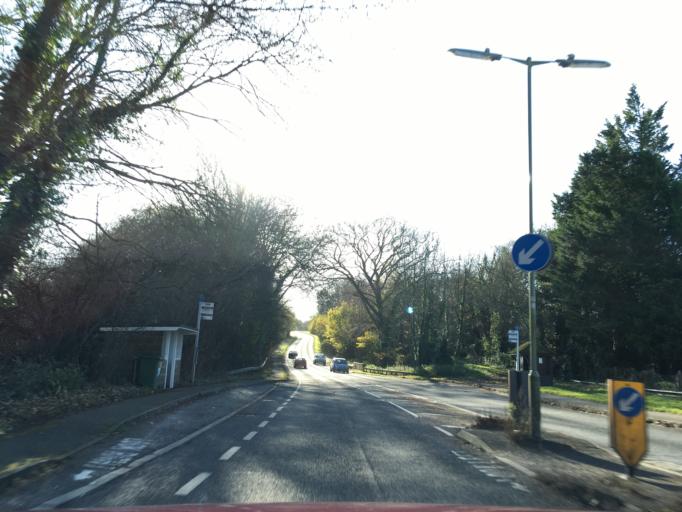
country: GB
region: England
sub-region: Hampshire
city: Compton
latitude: 51.0285
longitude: -1.3317
